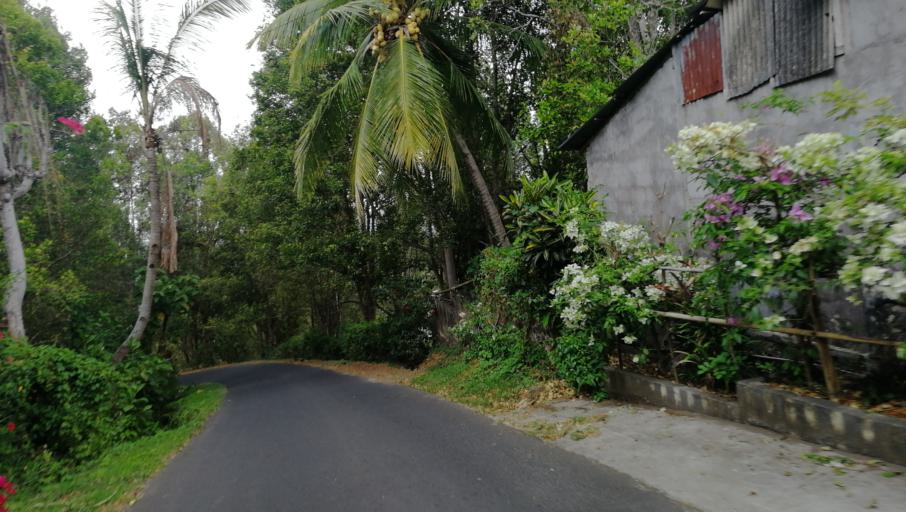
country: ID
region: Bali
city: Puspajati
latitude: -8.2776
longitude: 115.0279
